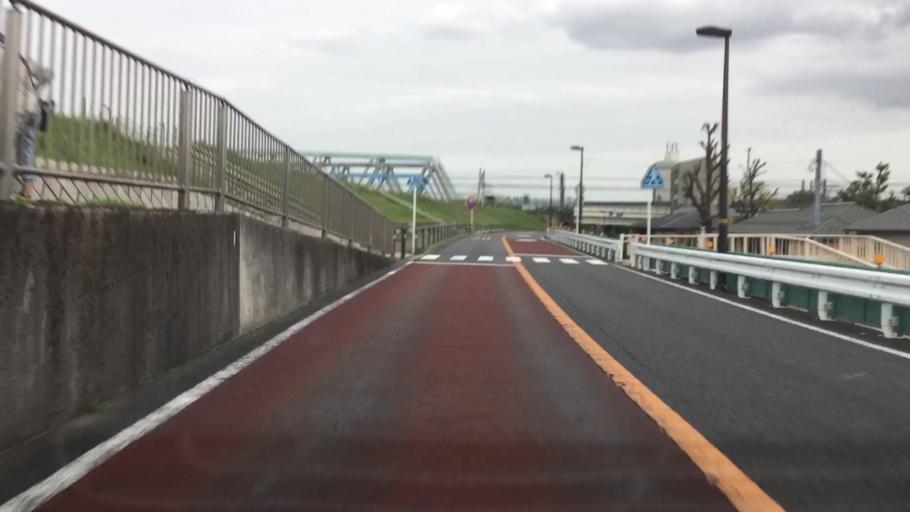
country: JP
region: Saitama
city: Soka
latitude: 35.7561
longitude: 139.8054
